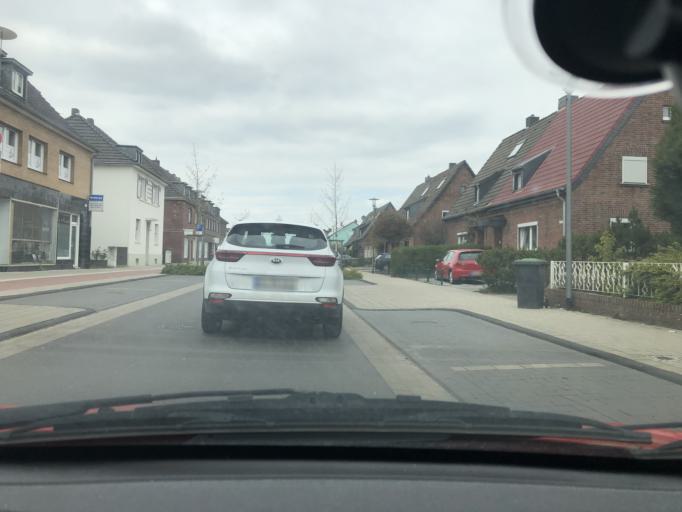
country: DE
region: North Rhine-Westphalia
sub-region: Regierungsbezirk Dusseldorf
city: Kamp-Lintfort
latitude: 51.4958
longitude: 6.5346
